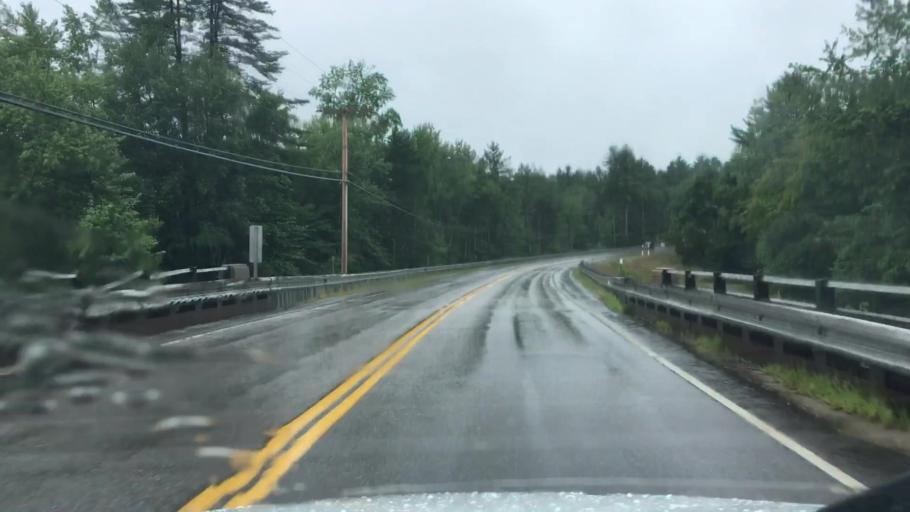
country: US
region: Maine
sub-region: Oxford County
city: Fryeburg
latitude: 43.9918
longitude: -71.0474
